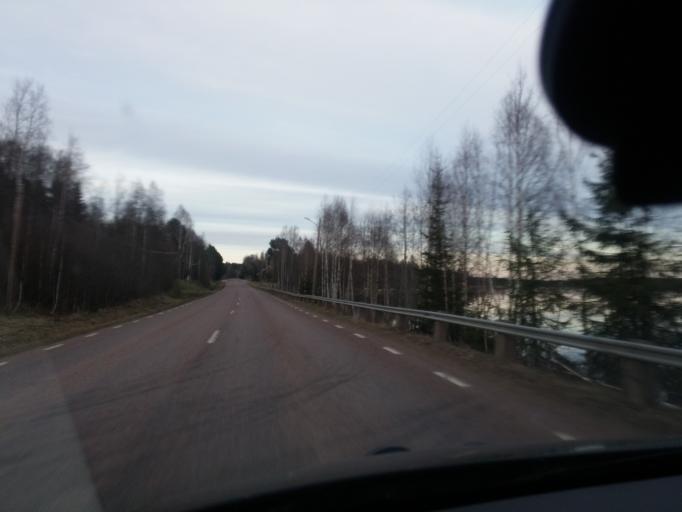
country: SE
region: Dalarna
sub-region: Faluns Kommun
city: Bjursas
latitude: 60.7139
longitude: 15.3204
